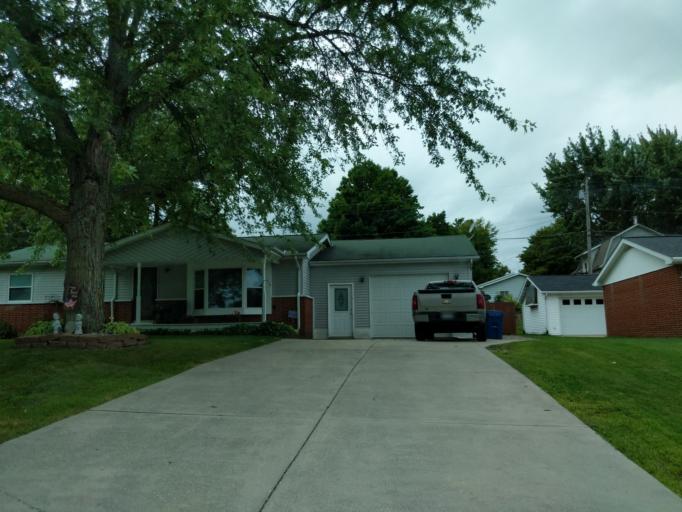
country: US
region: Michigan
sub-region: Lapeer County
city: Barnes Lake-Millers Lake
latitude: 43.3326
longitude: -83.3503
